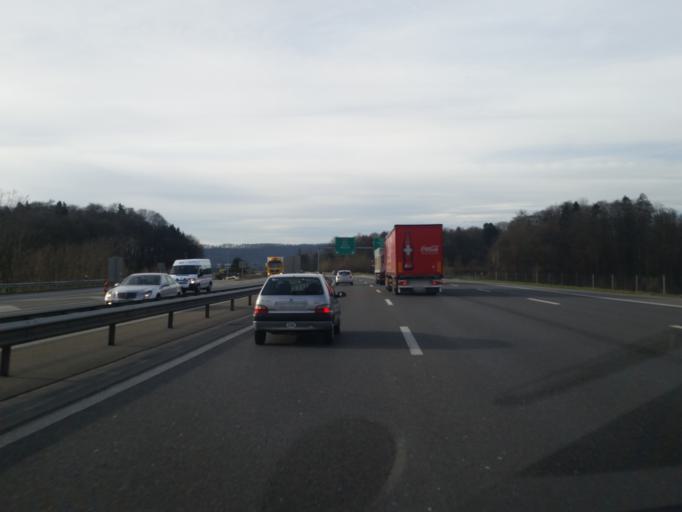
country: CH
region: Aargau
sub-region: Bezirk Baden
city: Birmenstorf
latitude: 47.4486
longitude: 8.2516
